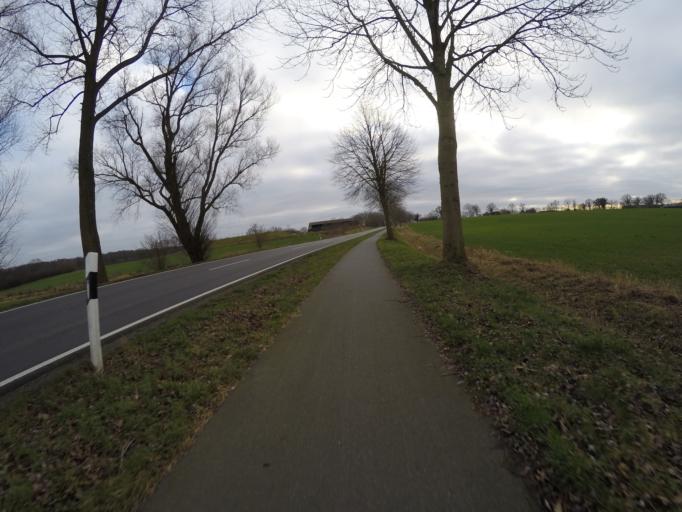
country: DE
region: Schleswig-Holstein
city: Alveslohe
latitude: 53.7812
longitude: 9.9089
